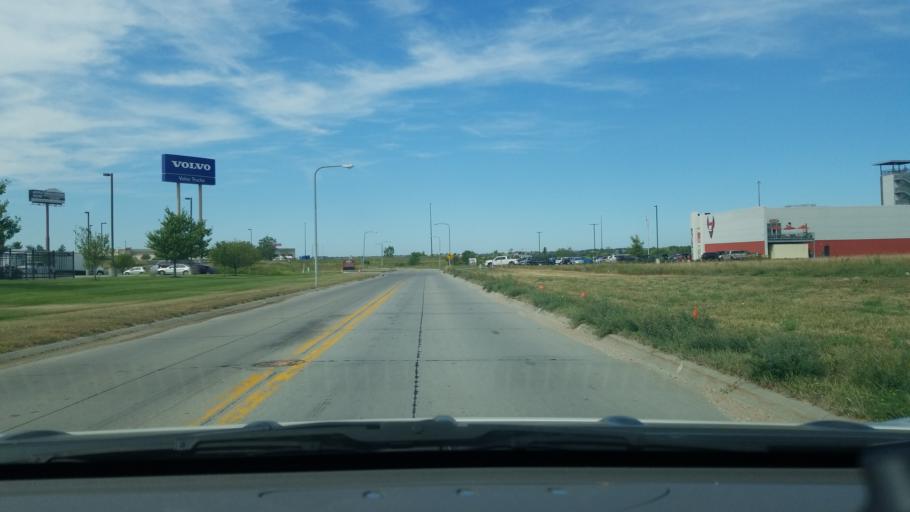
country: US
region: Nebraska
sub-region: Sarpy County
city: Chalco
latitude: 41.1455
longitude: -96.1536
